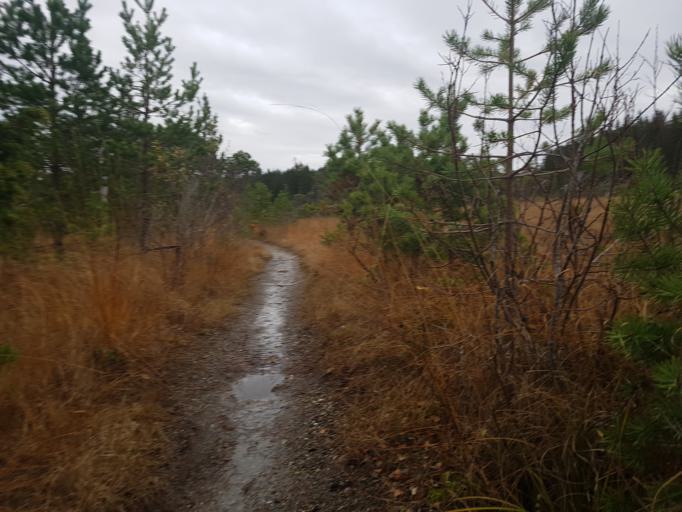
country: NO
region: Sor-Trondelag
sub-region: Melhus
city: Melhus
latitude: 63.3836
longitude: 10.2473
